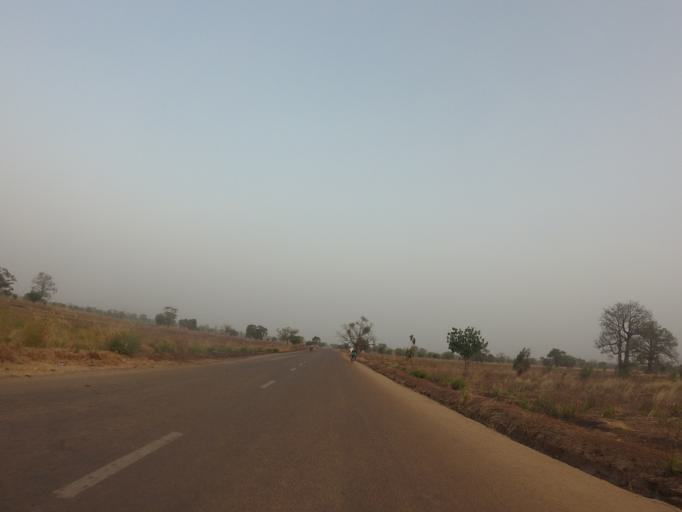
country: GH
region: Northern
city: Tamale
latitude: 9.4431
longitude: -1.1096
